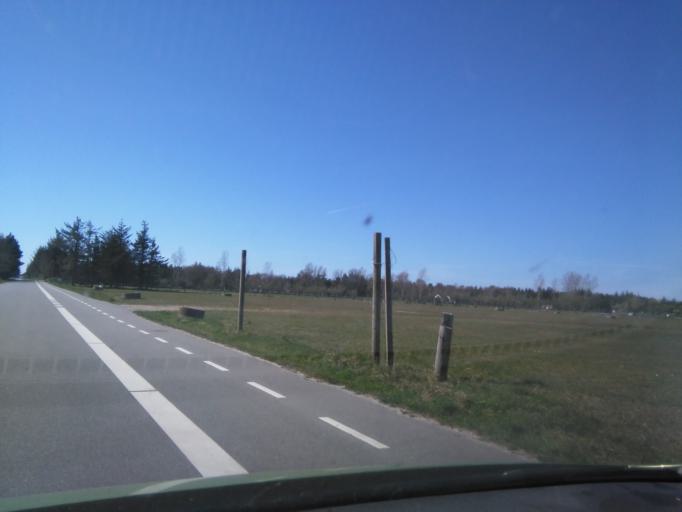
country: DK
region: South Denmark
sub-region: Varde Kommune
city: Oksbol
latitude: 55.5497
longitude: 8.2192
